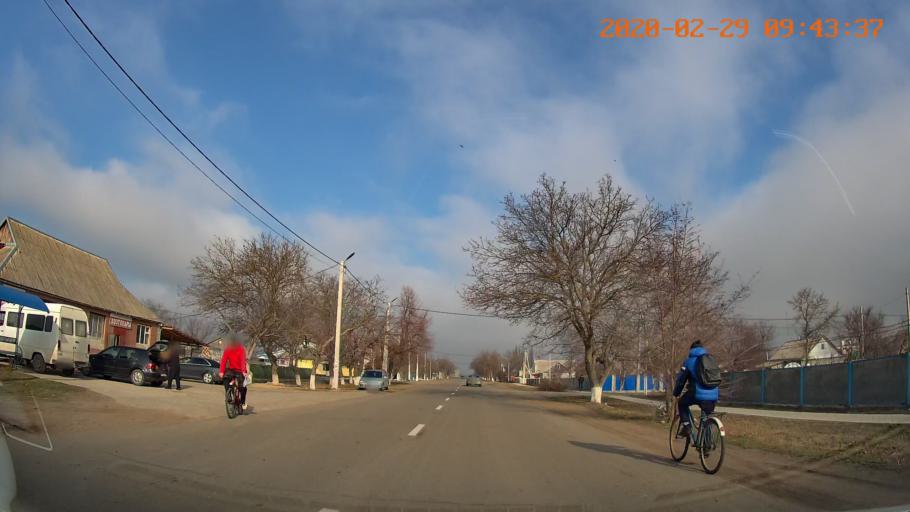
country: MD
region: Telenesti
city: Crasnoe
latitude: 46.6457
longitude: 29.8209
